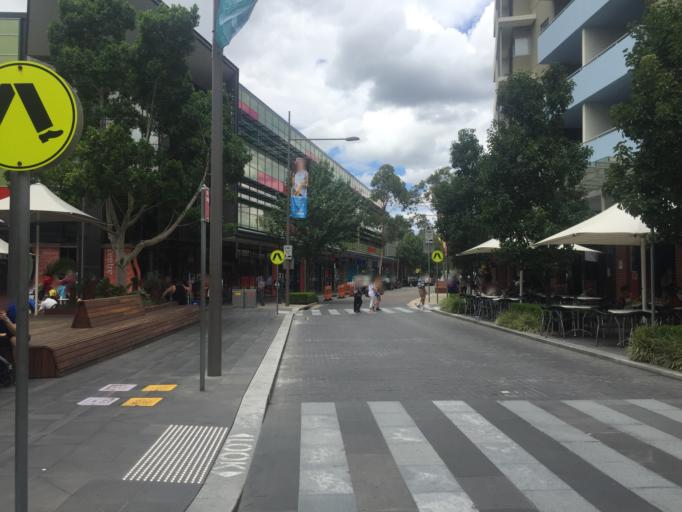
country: AU
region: New South Wales
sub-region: Blacktown
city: Rouse Hill
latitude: -33.6904
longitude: 150.9259
